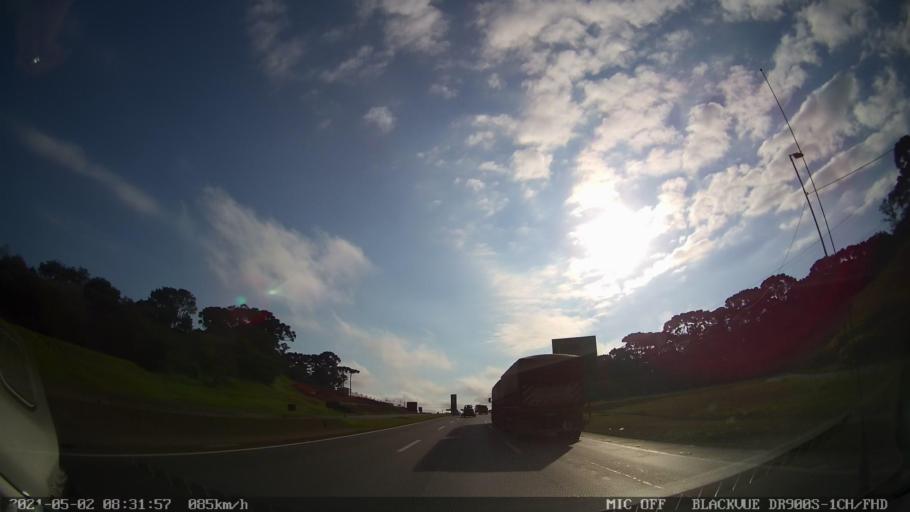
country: BR
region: Parana
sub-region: Piraquara
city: Piraquara
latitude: -25.4970
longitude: -49.1171
